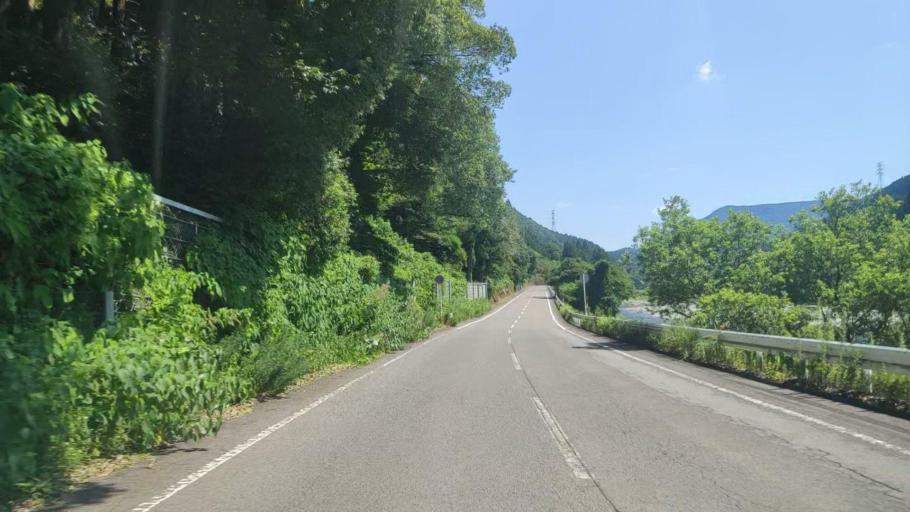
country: JP
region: Gifu
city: Godo
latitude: 35.6090
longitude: 136.6272
